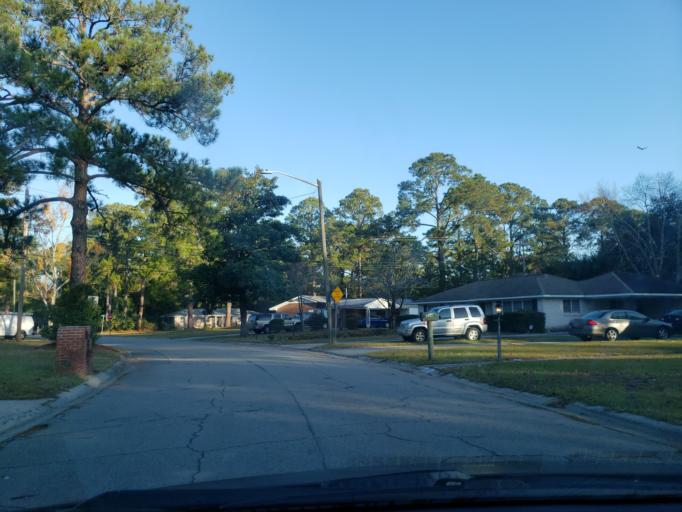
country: US
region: Georgia
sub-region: Chatham County
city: Montgomery
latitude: 31.9874
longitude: -81.1241
